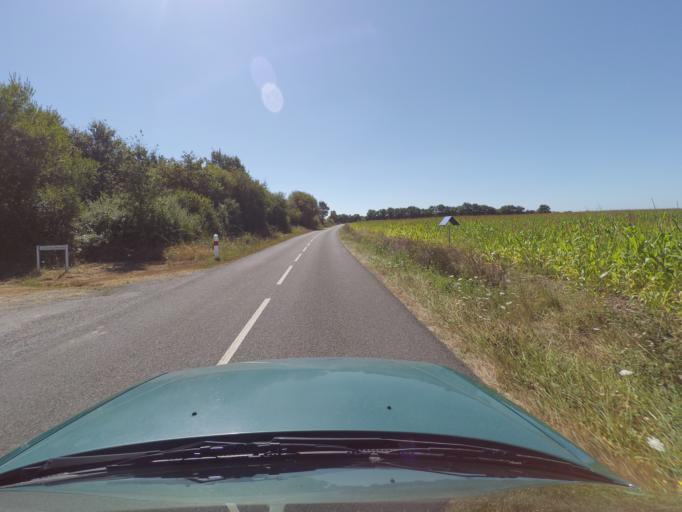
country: FR
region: Pays de la Loire
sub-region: Departement de la Loire-Atlantique
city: Le Bignon
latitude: 47.1064
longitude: -1.4963
